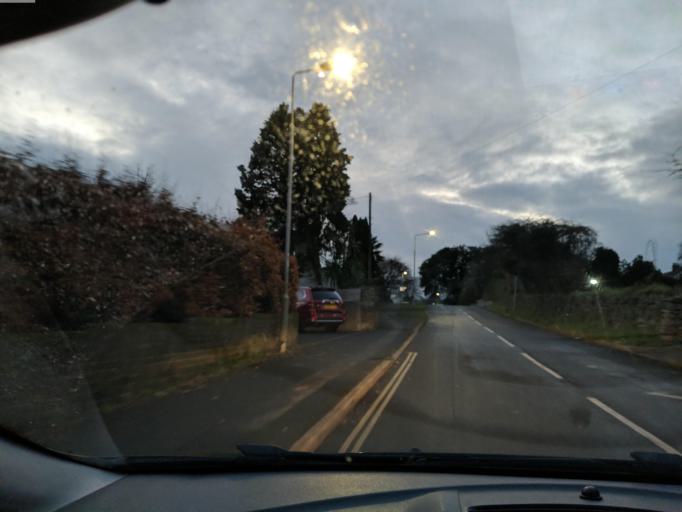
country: GB
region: England
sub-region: Plymouth
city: Plymouth
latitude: 50.3802
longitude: -4.1575
